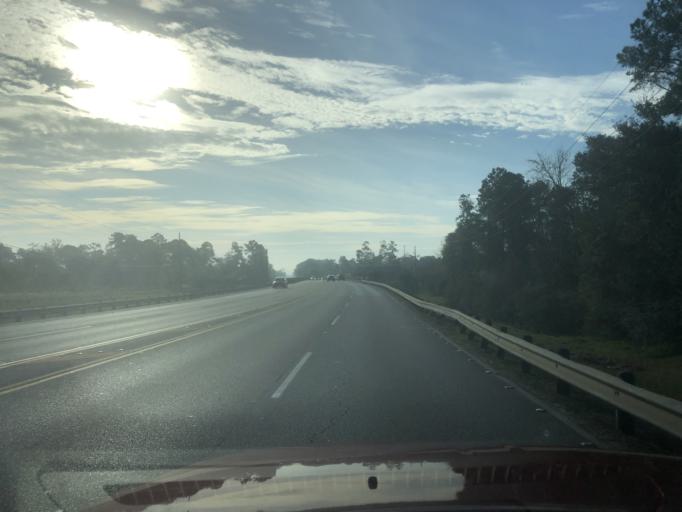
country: US
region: Texas
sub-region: Harris County
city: Spring
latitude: 30.0261
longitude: -95.4774
